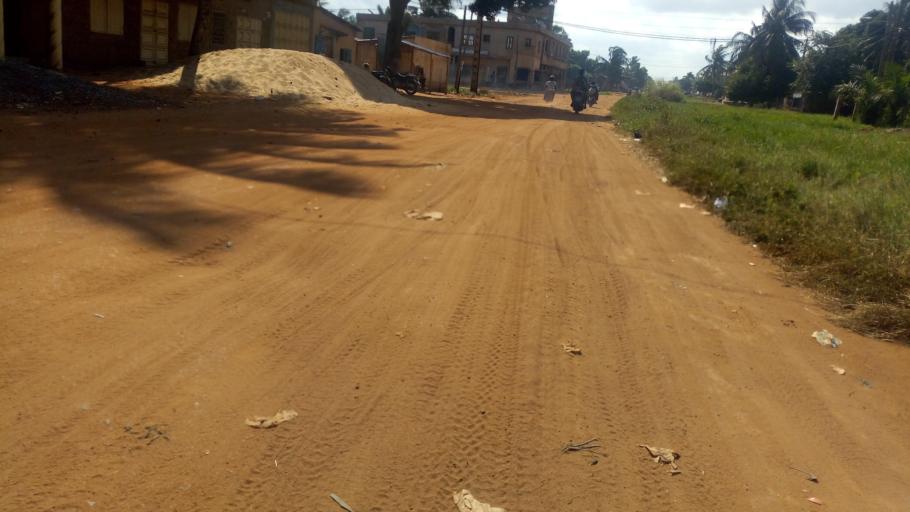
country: TG
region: Maritime
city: Lome
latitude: 6.2256
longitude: 1.1872
